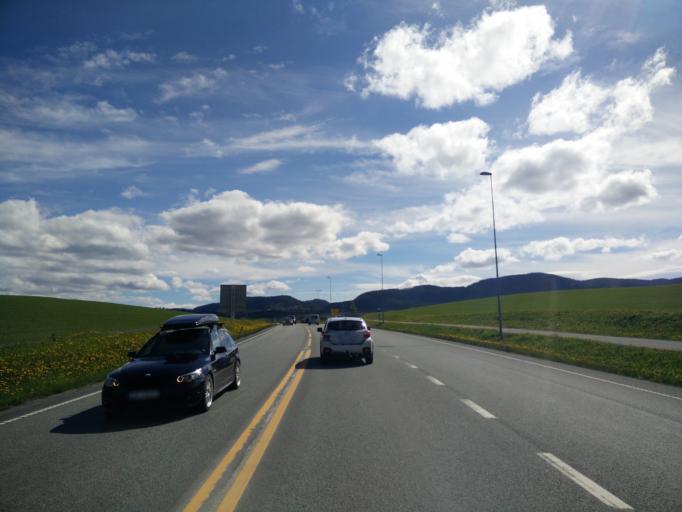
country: NO
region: Sor-Trondelag
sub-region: Melhus
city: Melhus
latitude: 63.3220
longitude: 10.3061
